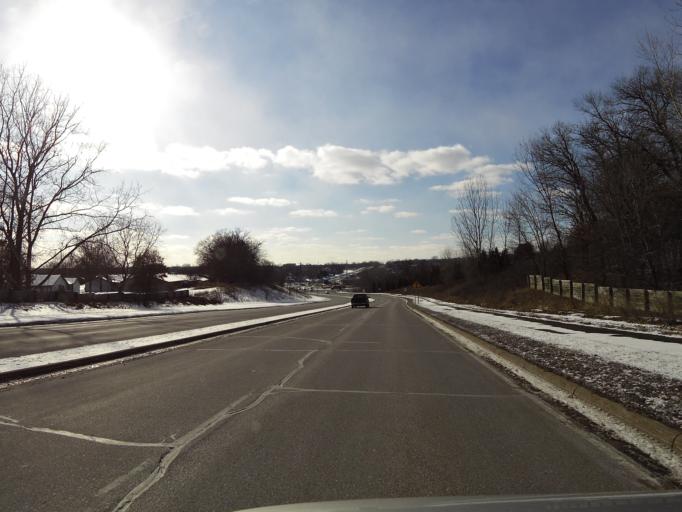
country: US
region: Minnesota
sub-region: Dakota County
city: Apple Valley
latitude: 44.7552
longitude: -93.2432
